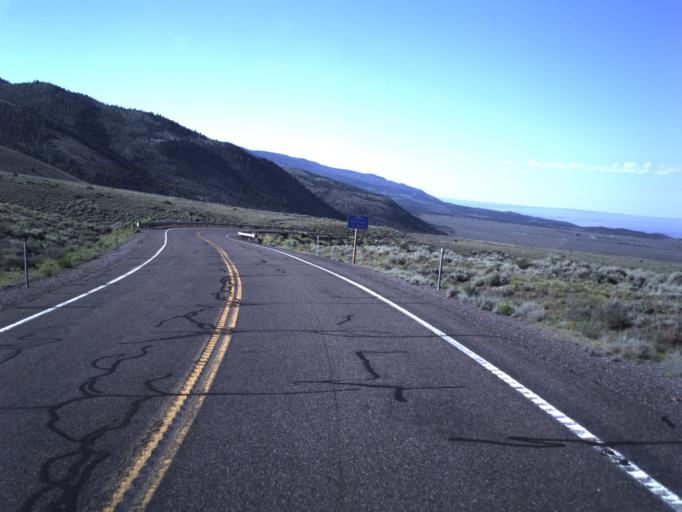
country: US
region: Utah
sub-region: Wayne County
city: Loa
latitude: 38.5494
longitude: -111.5105
